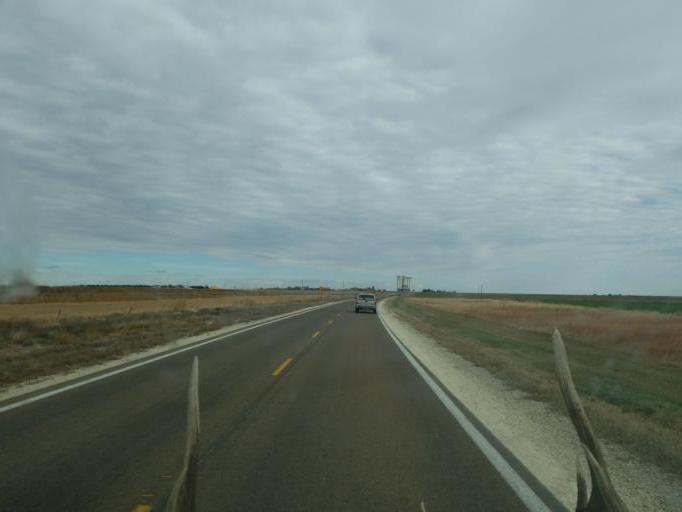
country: US
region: Kansas
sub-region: Logan County
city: Oakley
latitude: 39.0851
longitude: -101.1686
